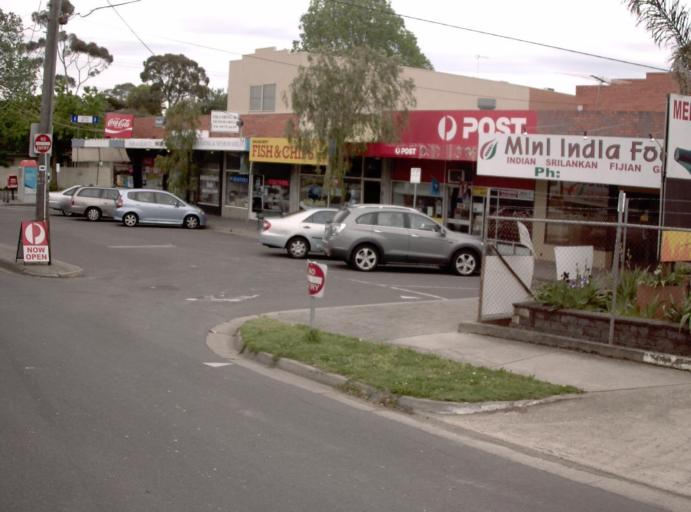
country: AU
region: Victoria
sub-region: Knox
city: Wantirna
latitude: -37.8294
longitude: 145.2272
